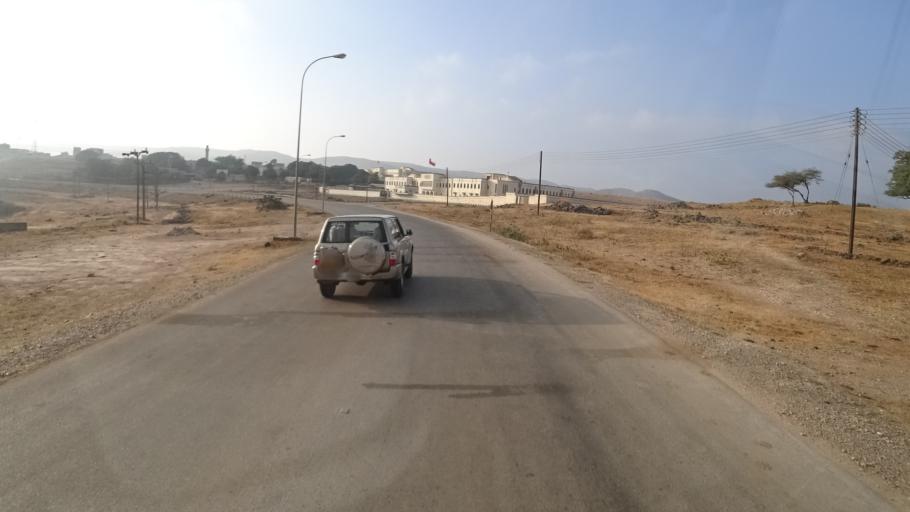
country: OM
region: Zufar
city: Salalah
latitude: 17.1250
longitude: 53.9983
